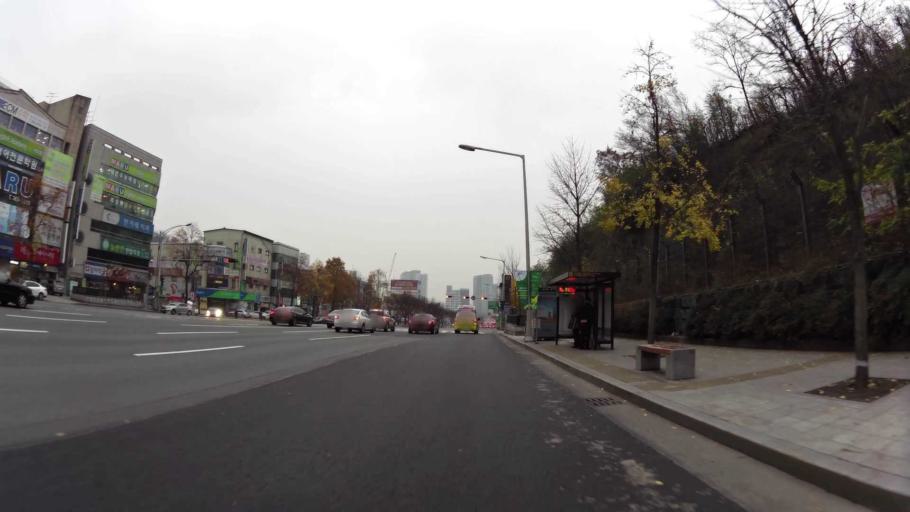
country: KR
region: Daegu
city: Daegu
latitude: 35.8549
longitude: 128.6536
